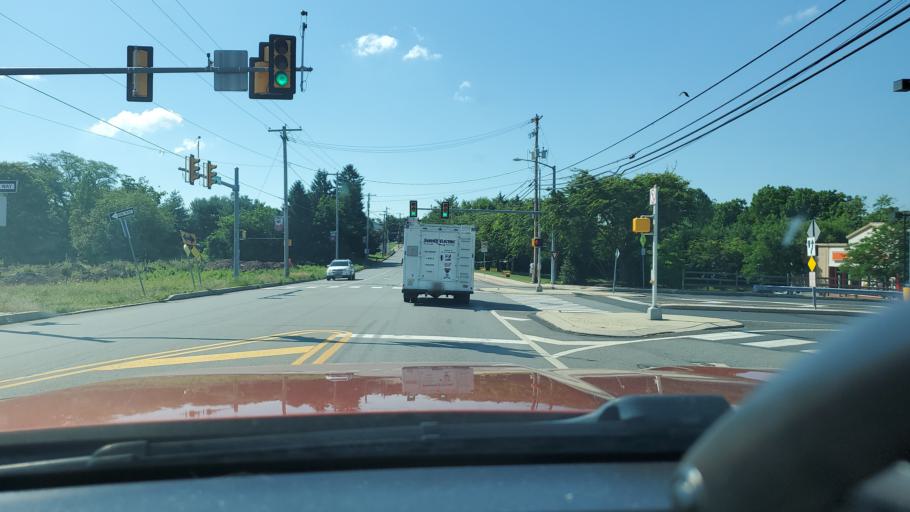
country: US
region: Pennsylvania
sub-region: Montgomery County
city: East Greenville
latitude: 40.4127
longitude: -75.5077
